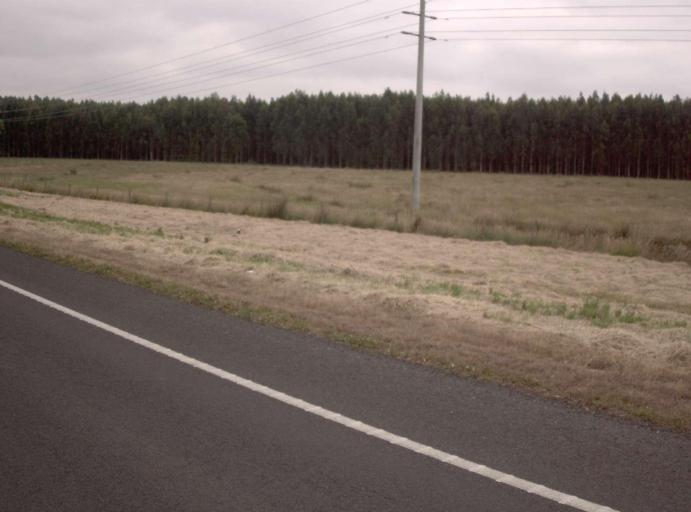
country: AU
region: Victoria
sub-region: Latrobe
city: Morwell
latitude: -38.2385
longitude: 146.3439
